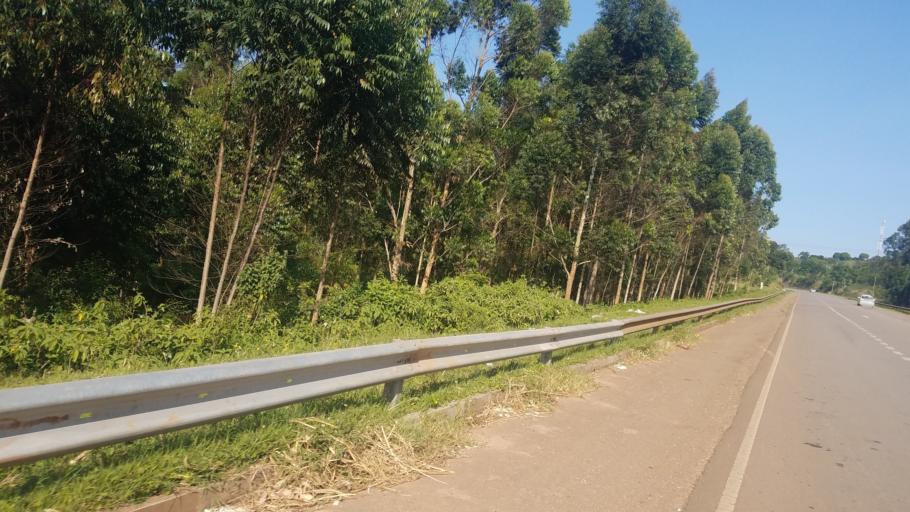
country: UG
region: Central Region
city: Masaka
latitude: -0.3373
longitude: 31.6848
